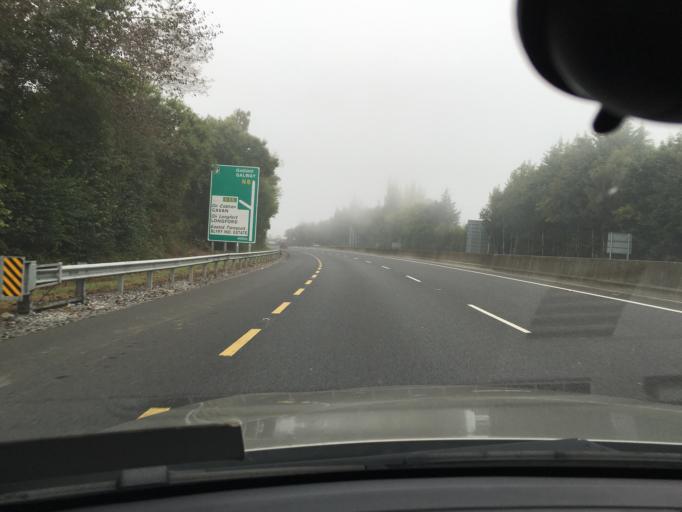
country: IE
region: Leinster
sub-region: An Iarmhi
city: Athlone
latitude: 53.4221
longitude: -7.8920
